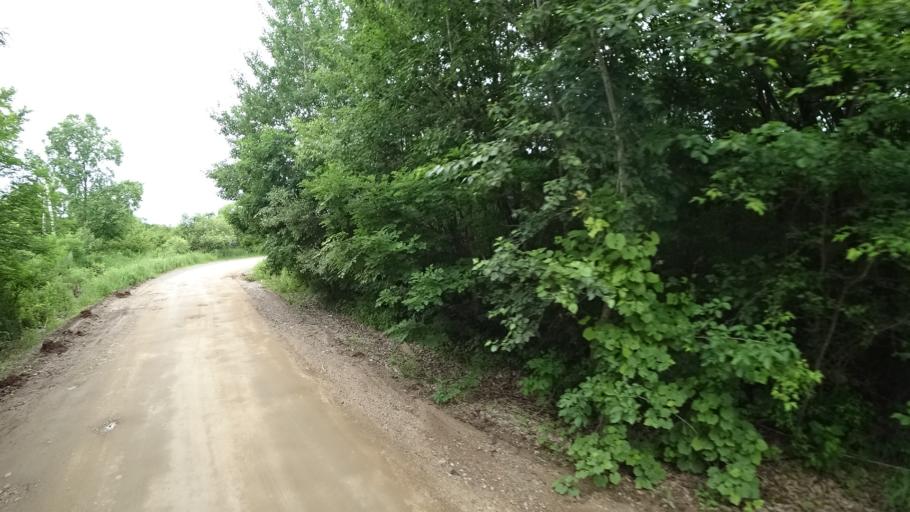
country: RU
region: Primorskiy
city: Arsen'yev
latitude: 44.1909
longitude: 133.3102
